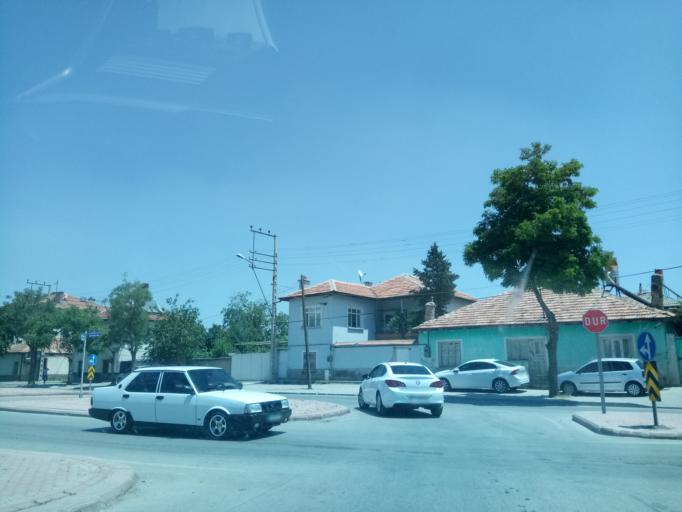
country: TR
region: Konya
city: Konya
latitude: 37.8440
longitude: 32.4955
